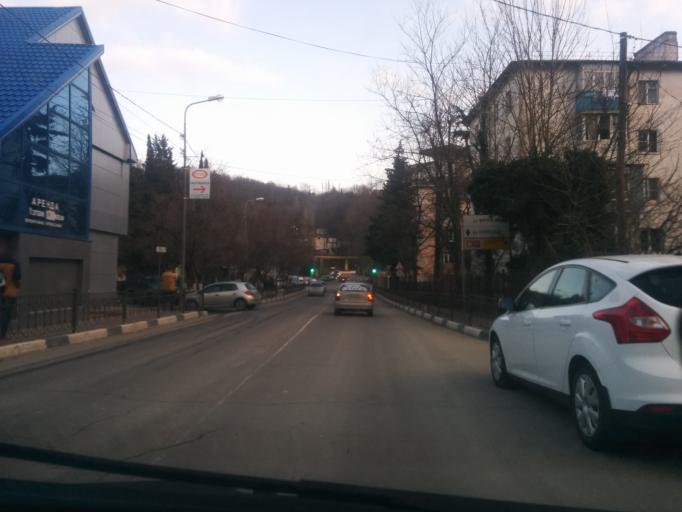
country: RU
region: Krasnodarskiy
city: Tuapse
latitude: 44.1120
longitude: 39.0601
